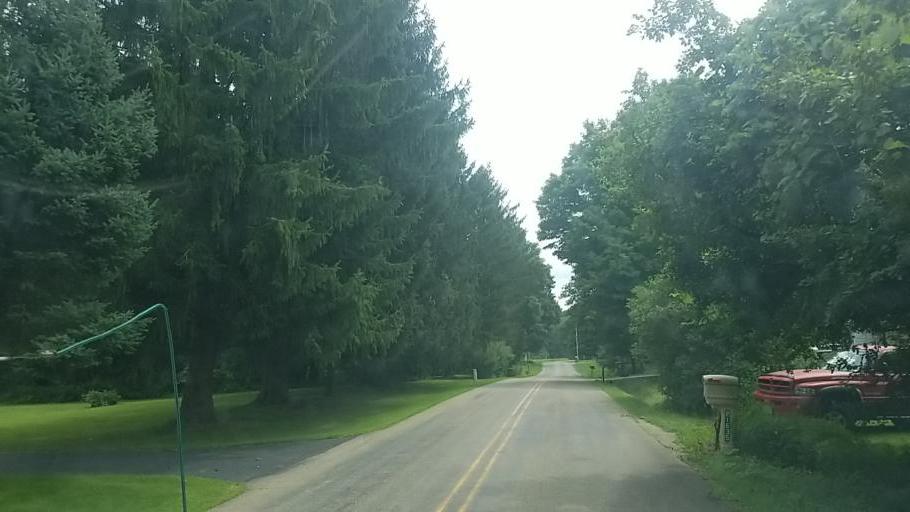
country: US
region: Ohio
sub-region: Knox County
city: Gambier
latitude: 40.3953
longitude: -82.3613
